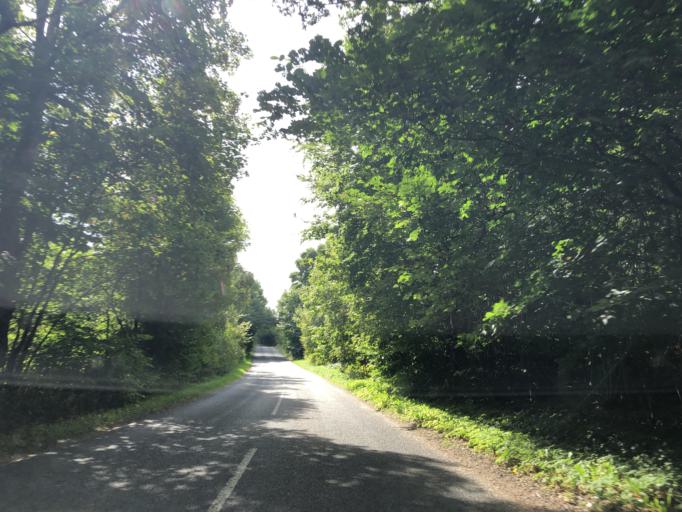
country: DK
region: North Denmark
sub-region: Vesthimmerland Kommune
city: Alestrup
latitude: 56.6048
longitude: 9.4343
